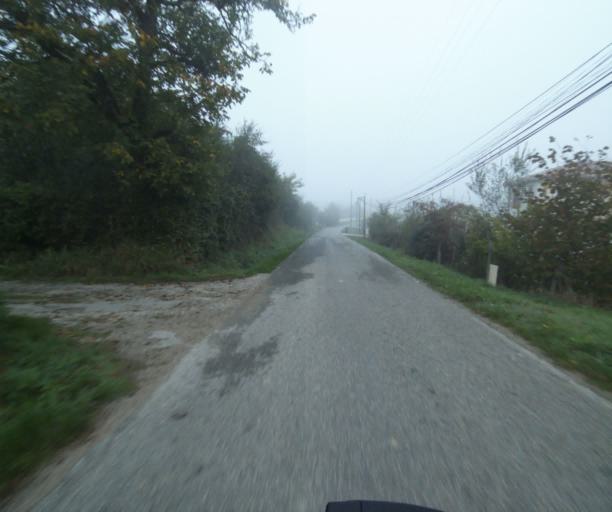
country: FR
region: Midi-Pyrenees
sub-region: Departement du Tarn-et-Garonne
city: Corbarieu
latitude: 43.9570
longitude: 1.3914
